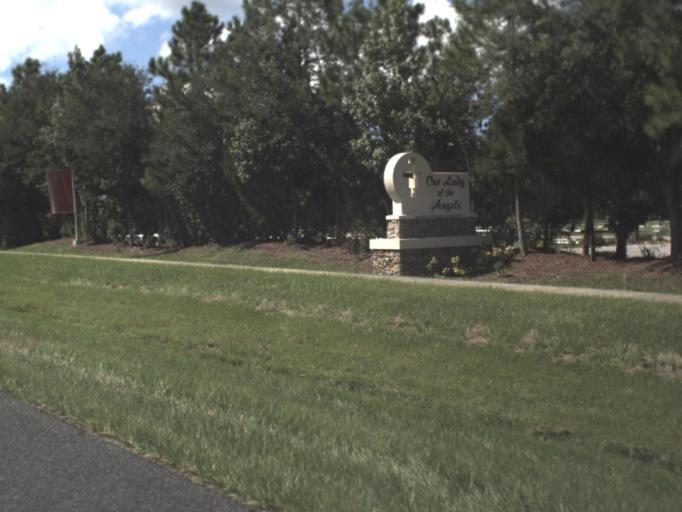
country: US
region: Florida
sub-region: Sarasota County
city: The Meadows
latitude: 27.4321
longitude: -82.4126
